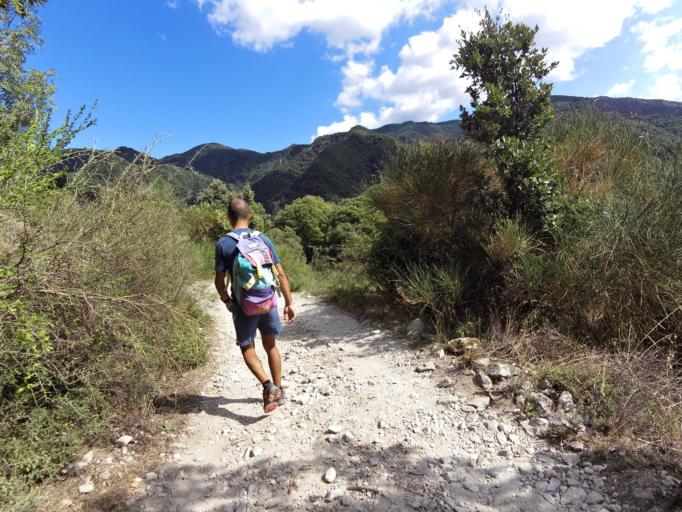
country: IT
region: Calabria
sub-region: Provincia di Reggio Calabria
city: Bivongi
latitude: 38.4921
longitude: 16.4059
